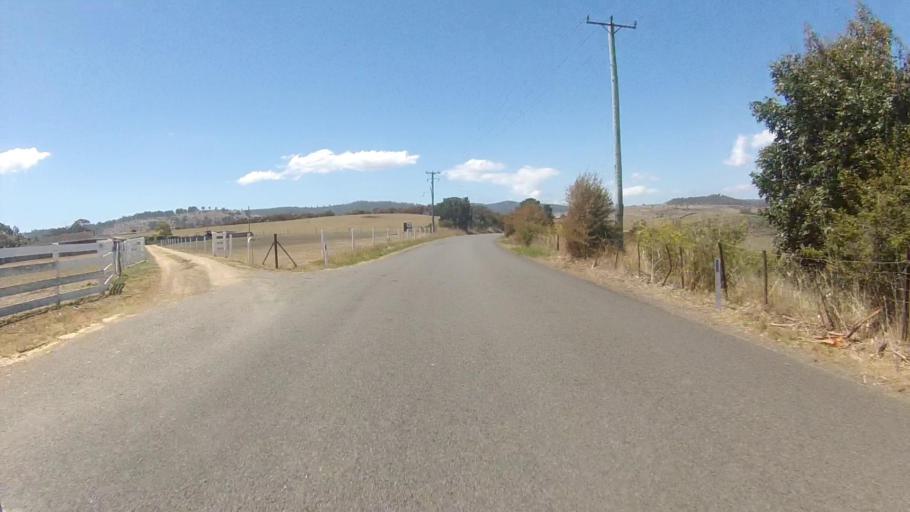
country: AU
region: Tasmania
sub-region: Sorell
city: Sorell
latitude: -42.7735
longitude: 147.5827
